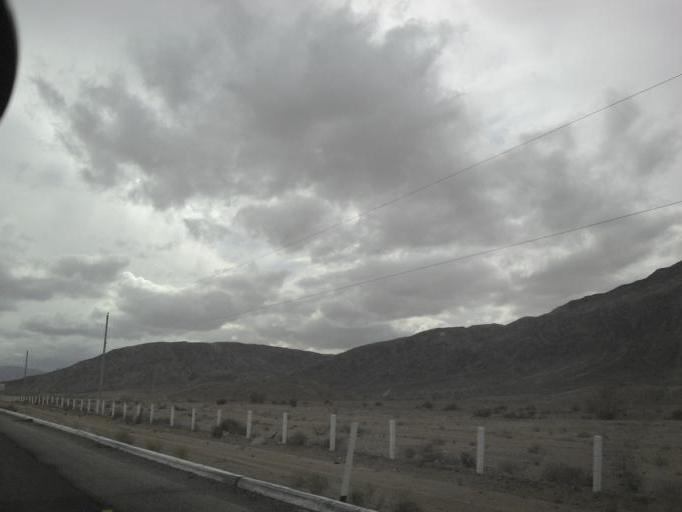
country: MX
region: Baja California
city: Progreso
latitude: 32.5907
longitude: -115.6967
